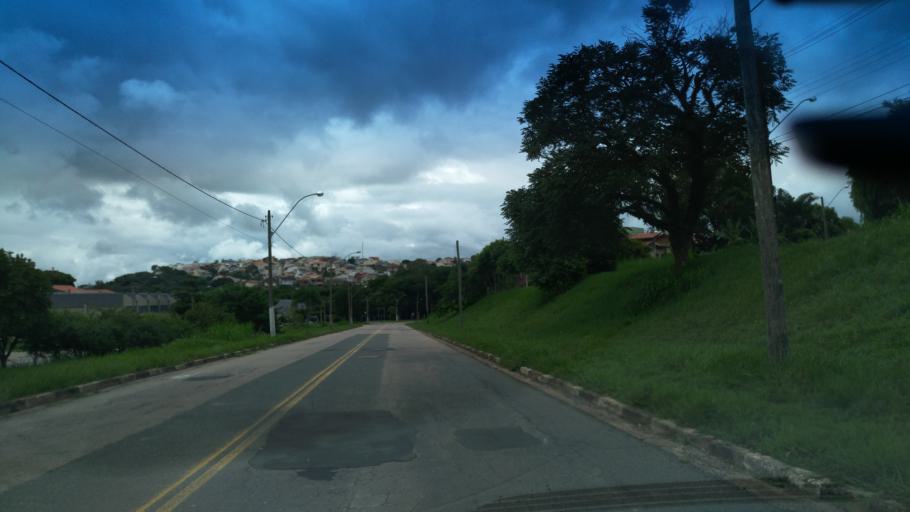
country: BR
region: Sao Paulo
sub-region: Valinhos
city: Valinhos
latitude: -22.9643
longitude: -46.9777
